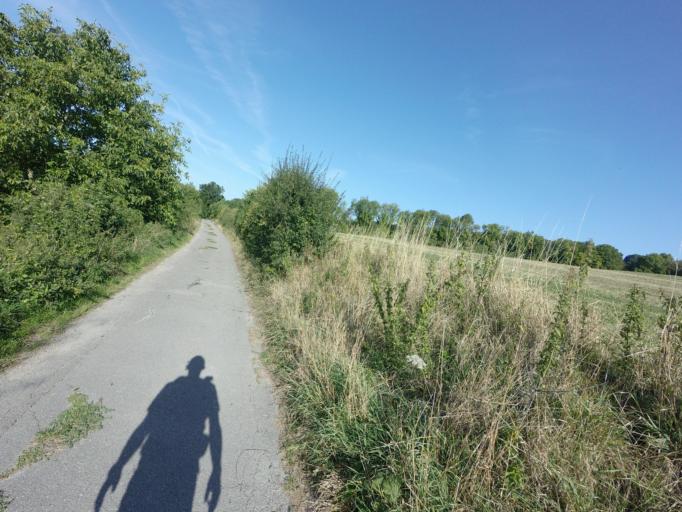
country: NL
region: Limburg
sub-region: Gemeente Vaals
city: Vaals
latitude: 50.7938
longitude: 5.9920
